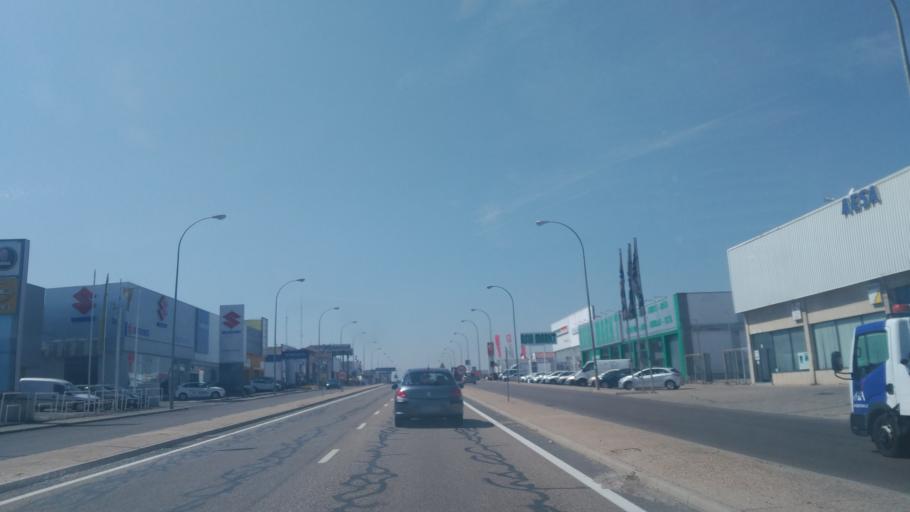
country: ES
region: Castille and Leon
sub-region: Provincia de Salamanca
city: Villares de la Reina
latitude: 40.9925
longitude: -5.6397
